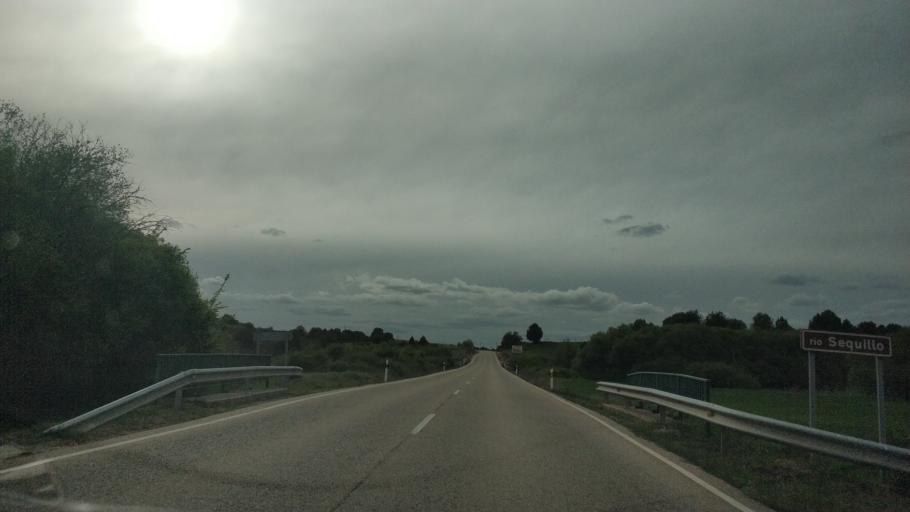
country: ES
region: Castille and Leon
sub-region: Provincia de Soria
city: Valdenebro
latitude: 41.5722
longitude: -3.0149
